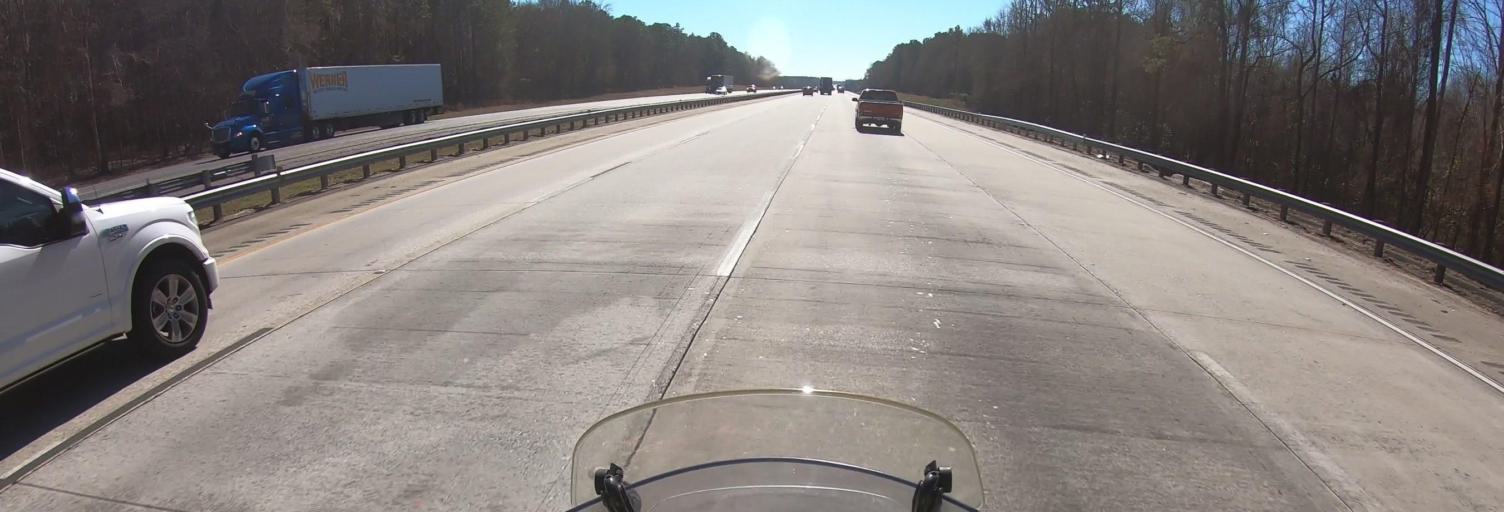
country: US
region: Georgia
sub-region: Dooly County
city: Unadilla
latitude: 32.3324
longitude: -83.7681
